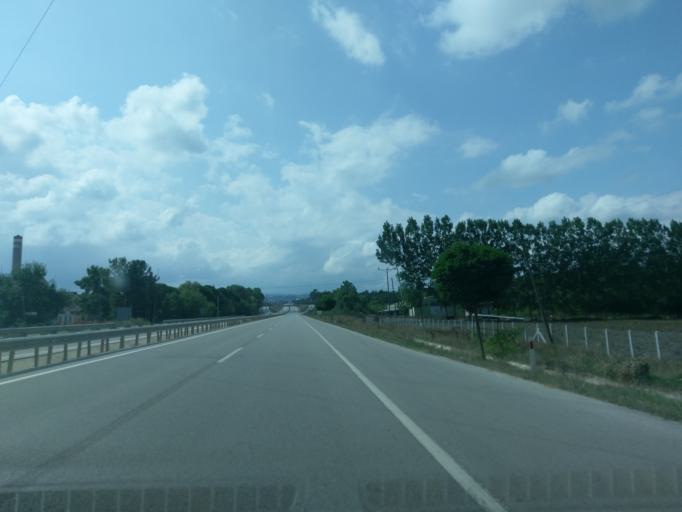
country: TR
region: Sinop
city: Kabali
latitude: 41.9246
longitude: 35.0808
